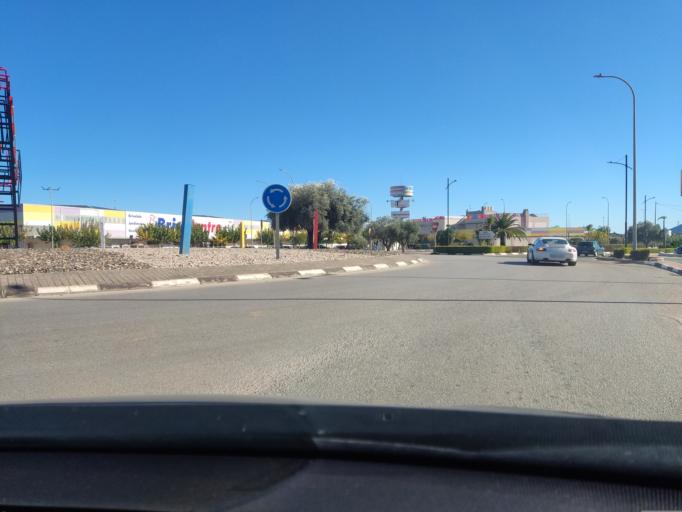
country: ES
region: Valencia
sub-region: Provincia de Alicante
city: Vergel
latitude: 38.8530
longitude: 0.0015
